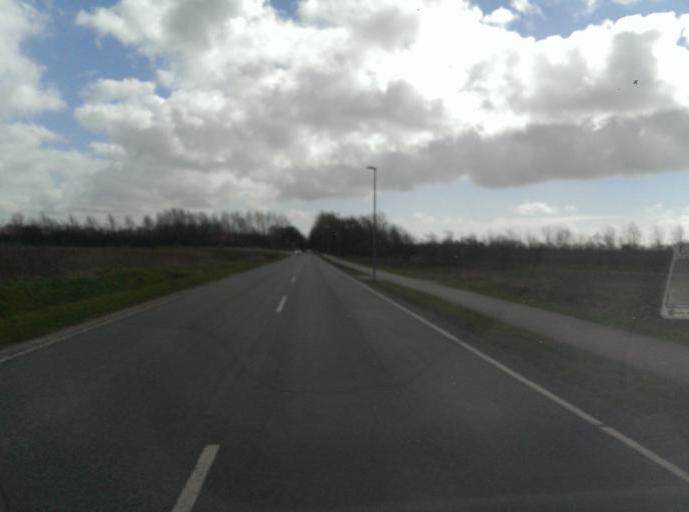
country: DK
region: South Denmark
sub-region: Esbjerg Kommune
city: Esbjerg
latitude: 55.5266
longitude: 8.4045
